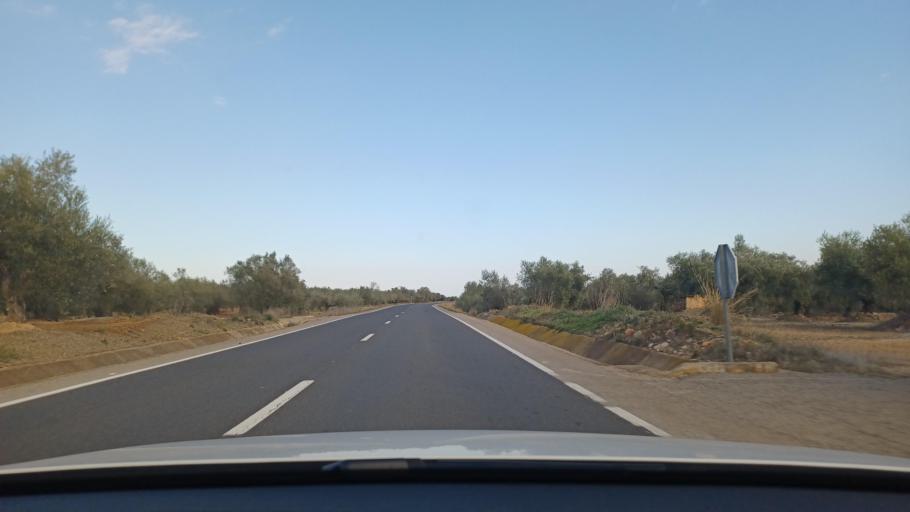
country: ES
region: Catalonia
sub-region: Provincia de Tarragona
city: Ulldecona
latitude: 40.6523
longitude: 0.3971
